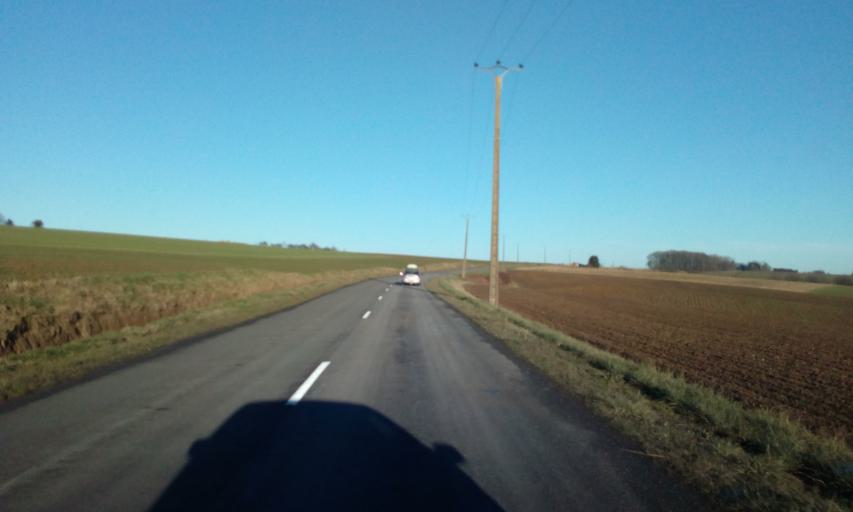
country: FR
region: Picardie
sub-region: Departement de l'Aisne
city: Rozoy-sur-Serre
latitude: 49.7120
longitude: 4.2305
